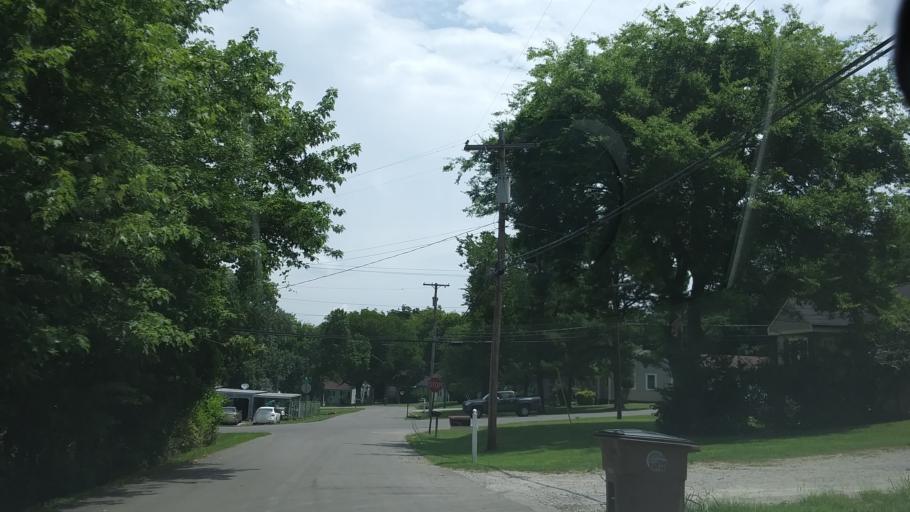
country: US
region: Tennessee
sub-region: Davidson County
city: Belle Meade
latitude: 36.1480
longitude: -86.8701
